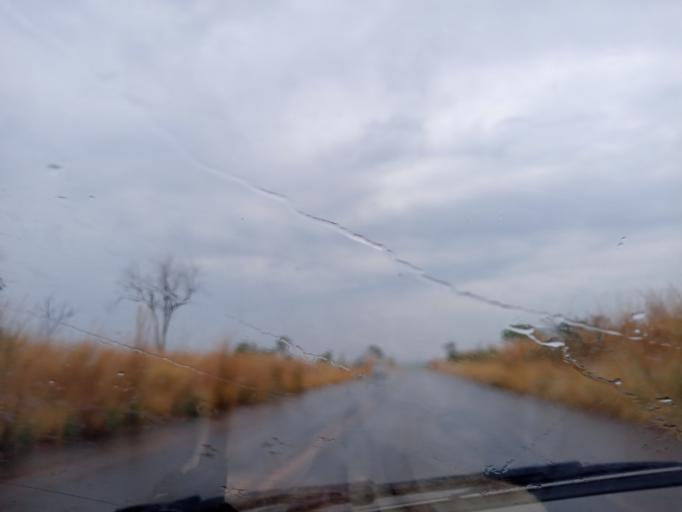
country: BR
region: Minas Gerais
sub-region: Ituiutaba
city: Ituiutaba
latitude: -19.1033
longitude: -49.5154
